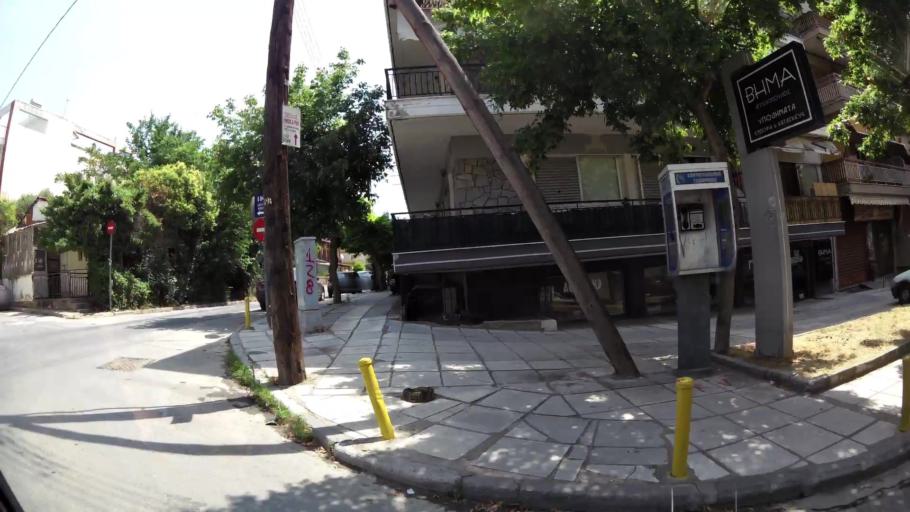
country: GR
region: Central Macedonia
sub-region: Nomos Thessalonikis
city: Evosmos
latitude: 40.6731
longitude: 22.8957
